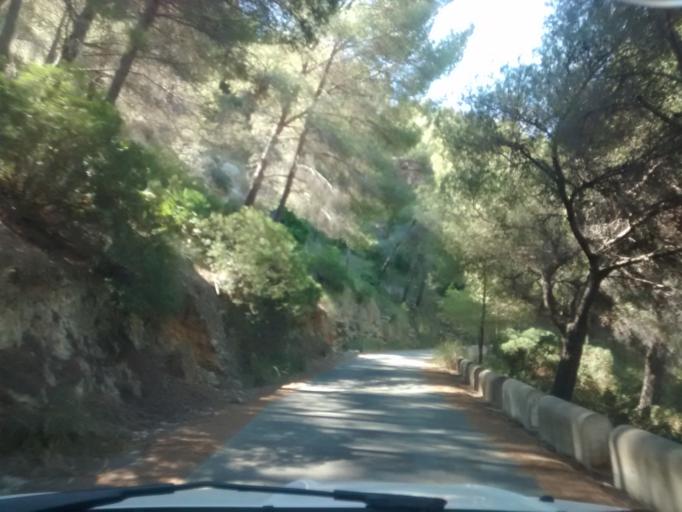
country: ES
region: Balearic Islands
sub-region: Illes Balears
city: Port d'Alcudia
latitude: 39.8788
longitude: 3.1756
